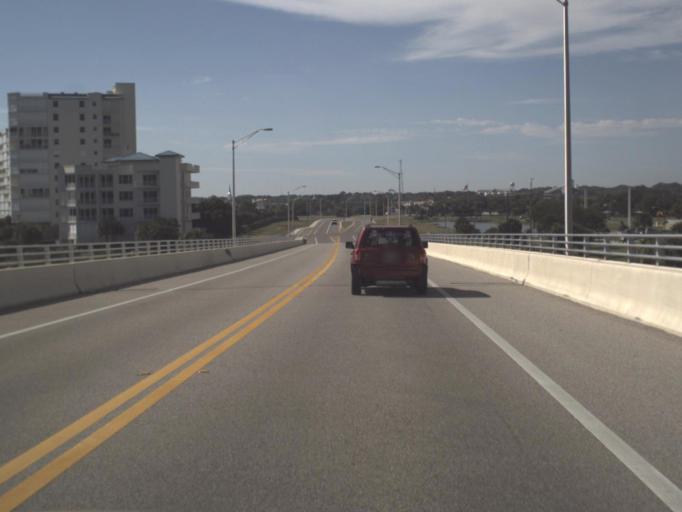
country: US
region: Florida
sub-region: Brevard County
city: Titusville
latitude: 28.6185
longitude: -80.8016
